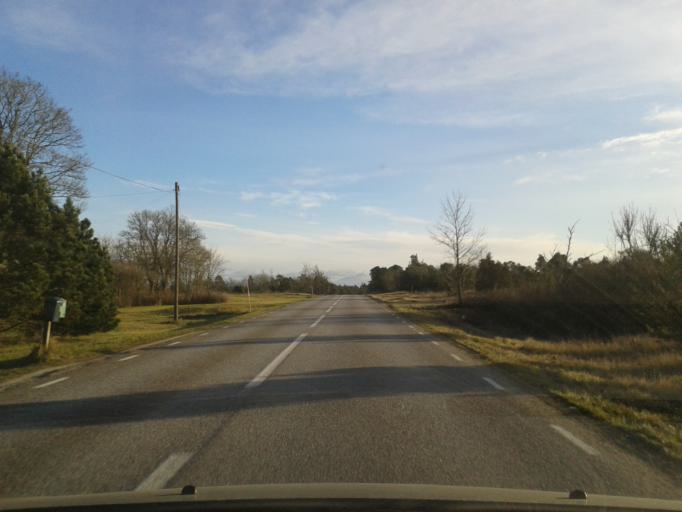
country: SE
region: Gotland
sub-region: Gotland
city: Hemse
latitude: 57.3661
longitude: 18.6728
